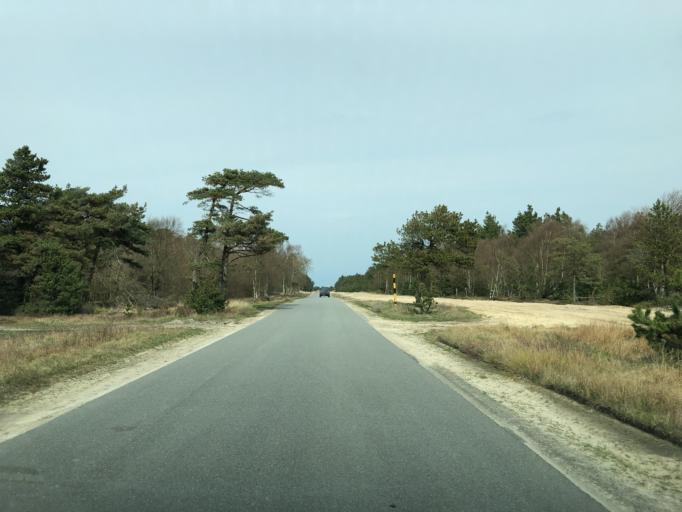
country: DK
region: South Denmark
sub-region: Varde Kommune
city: Oksbol
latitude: 55.6273
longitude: 8.1702
